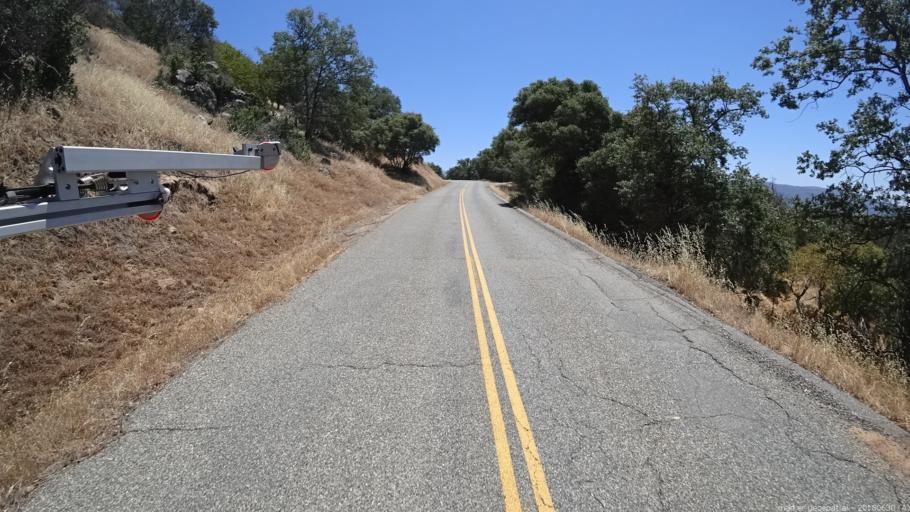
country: US
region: California
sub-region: Fresno County
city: Auberry
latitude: 37.1772
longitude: -119.4423
